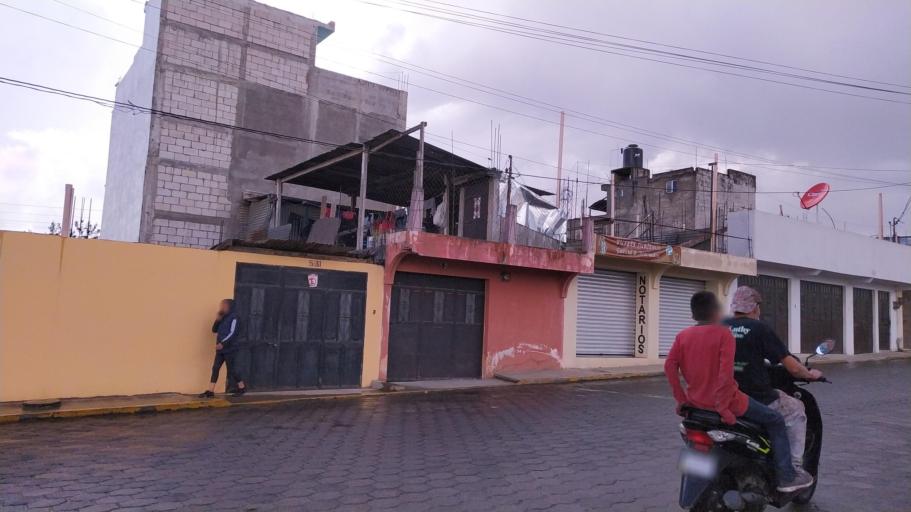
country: GT
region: Quetzaltenango
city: Quetzaltenango
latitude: 14.8543
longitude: -91.5082
